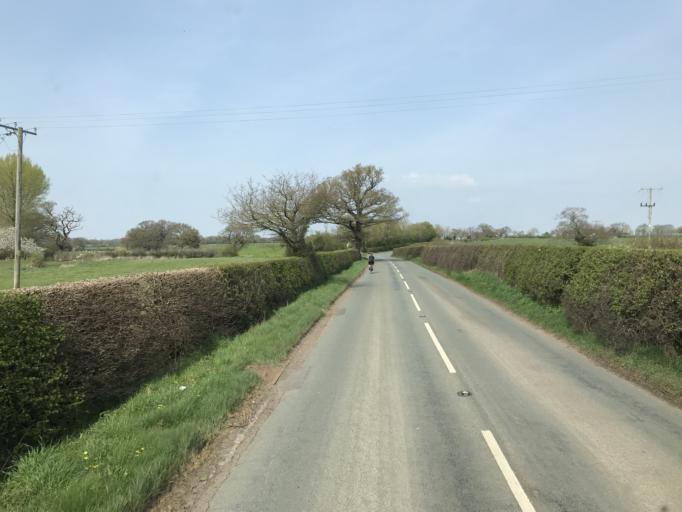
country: GB
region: England
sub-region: Cheshire West and Chester
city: Eccleston
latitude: 53.1519
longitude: -2.8619
